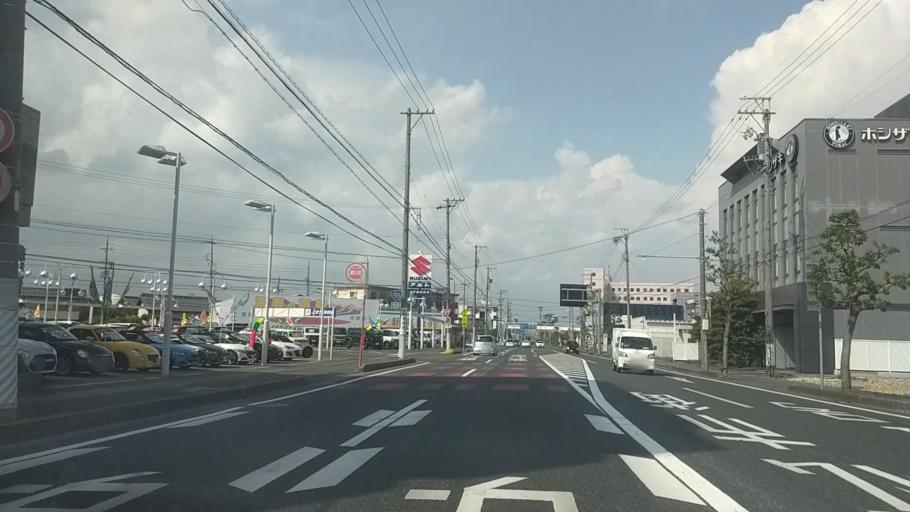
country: JP
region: Shizuoka
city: Hamamatsu
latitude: 34.7148
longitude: 137.7609
